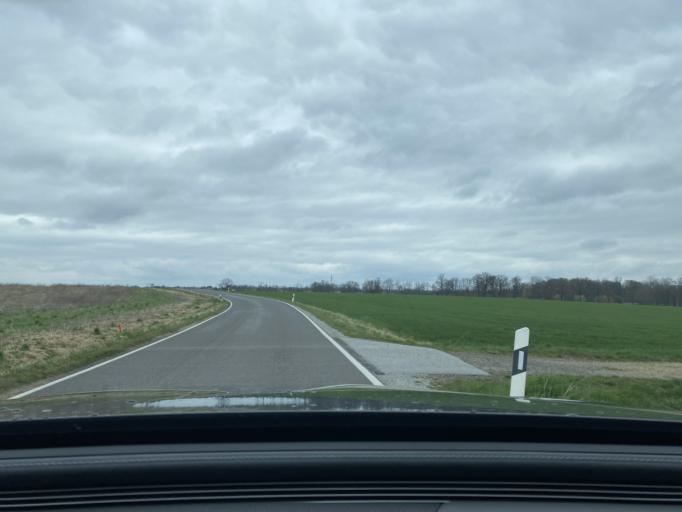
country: DE
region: Saxony
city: Neschwitz
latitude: 51.2545
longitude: 14.3338
